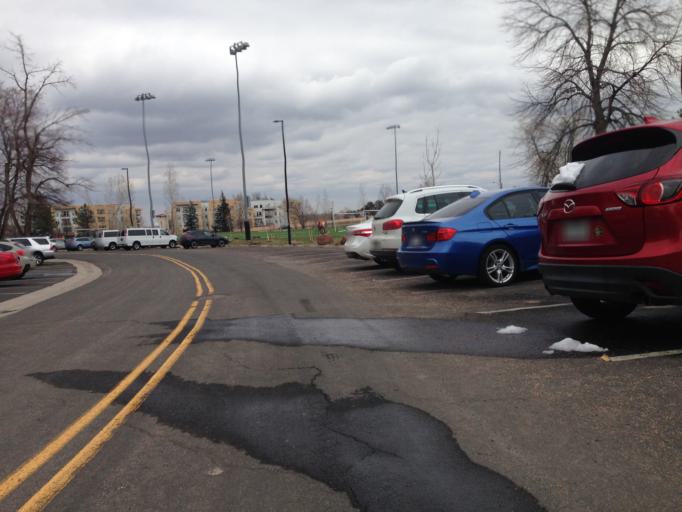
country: US
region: Colorado
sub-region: Boulder County
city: Boulder
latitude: 40.0016
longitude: -105.2614
